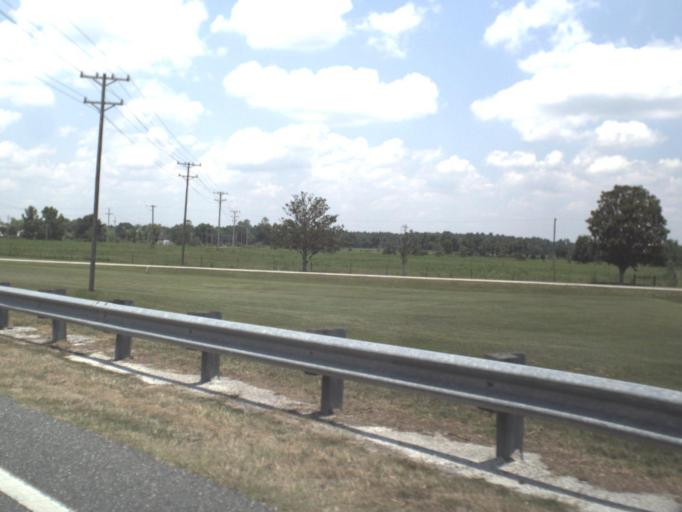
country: US
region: Florida
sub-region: Bradford County
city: Starke
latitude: 30.0692
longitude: -82.1860
